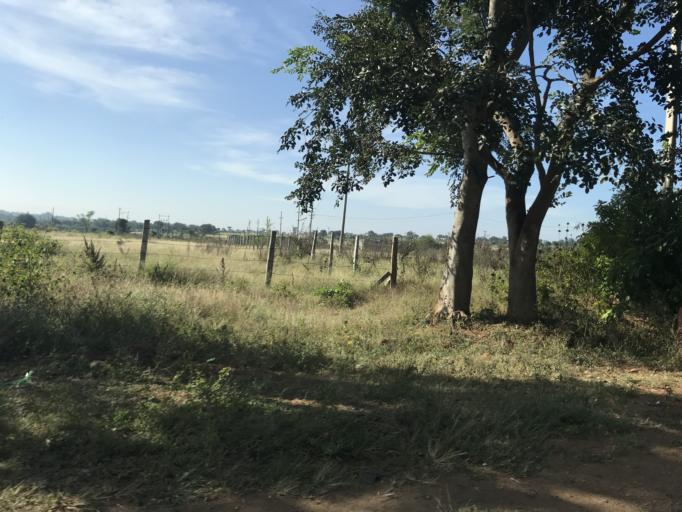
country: IN
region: Karnataka
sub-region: Mysore
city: Mysore
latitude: 12.2281
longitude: 76.5894
